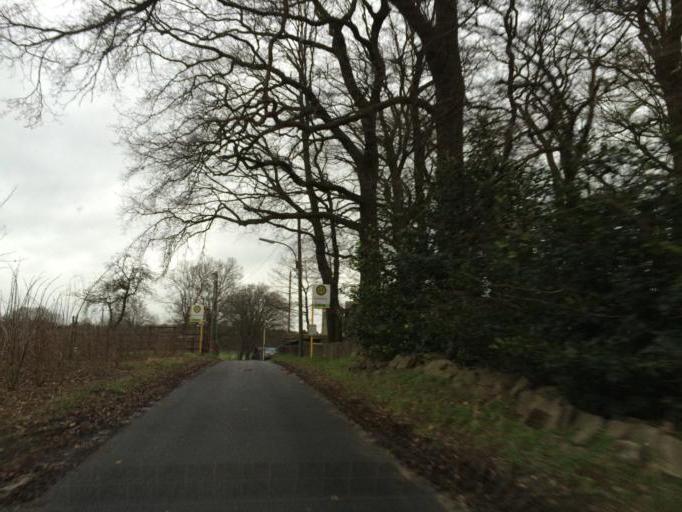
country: DE
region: North Rhine-Westphalia
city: Marl
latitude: 51.7028
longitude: 7.0736
